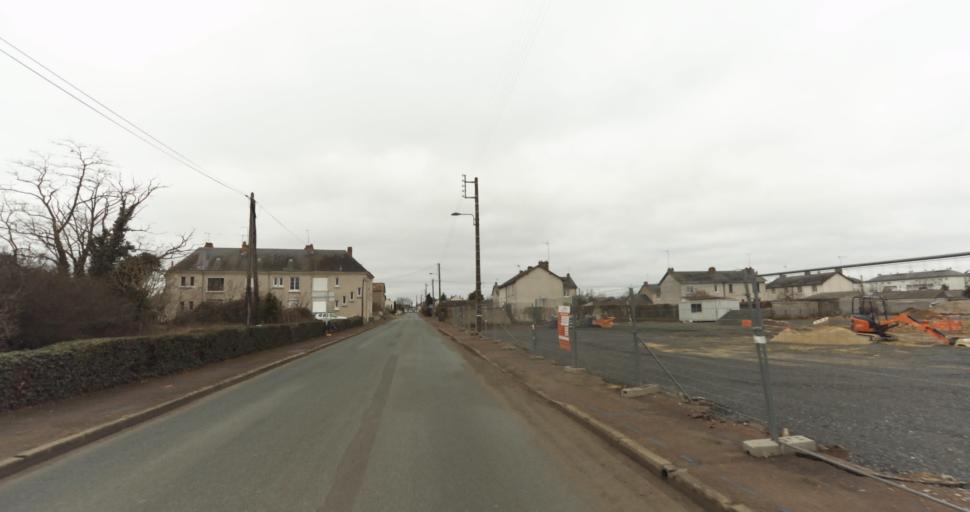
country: FR
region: Pays de la Loire
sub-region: Departement de Maine-et-Loire
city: Montreuil-Bellay
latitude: 47.1250
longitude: -0.1454
